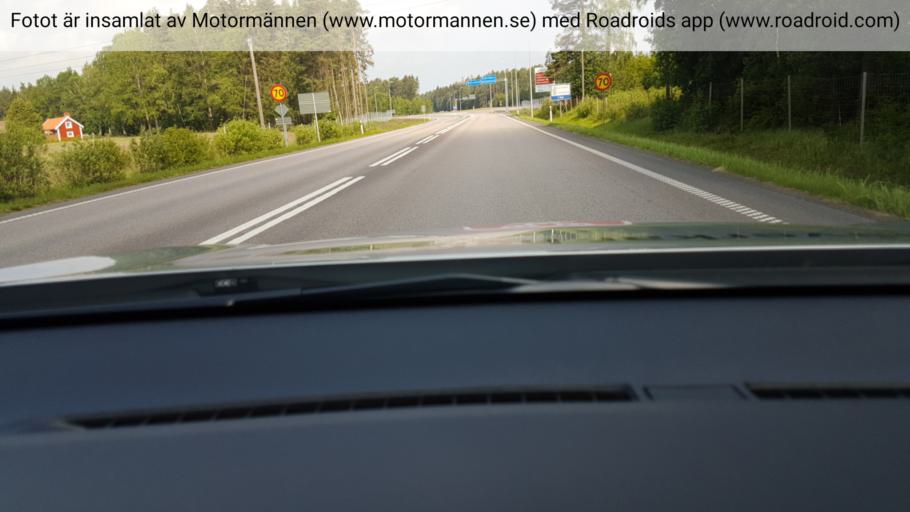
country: SE
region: Vaestra Goetaland
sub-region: Lidkopings Kommun
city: Lidkoping
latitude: 58.4767
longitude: 13.2049
